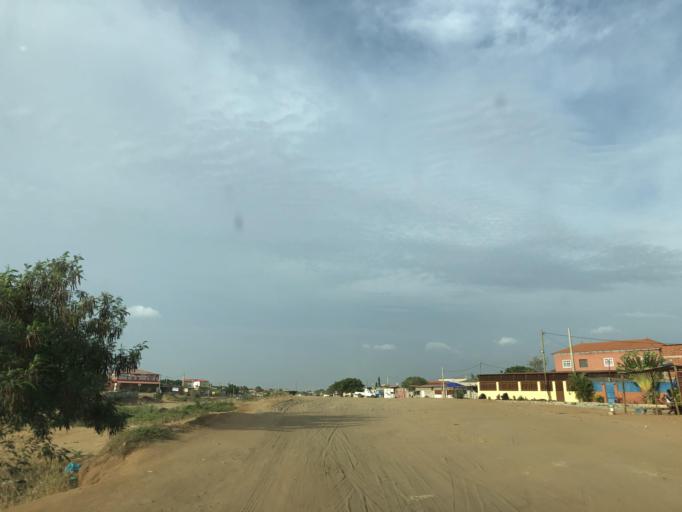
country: AO
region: Luanda
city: Luanda
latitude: -8.9234
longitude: 13.3067
